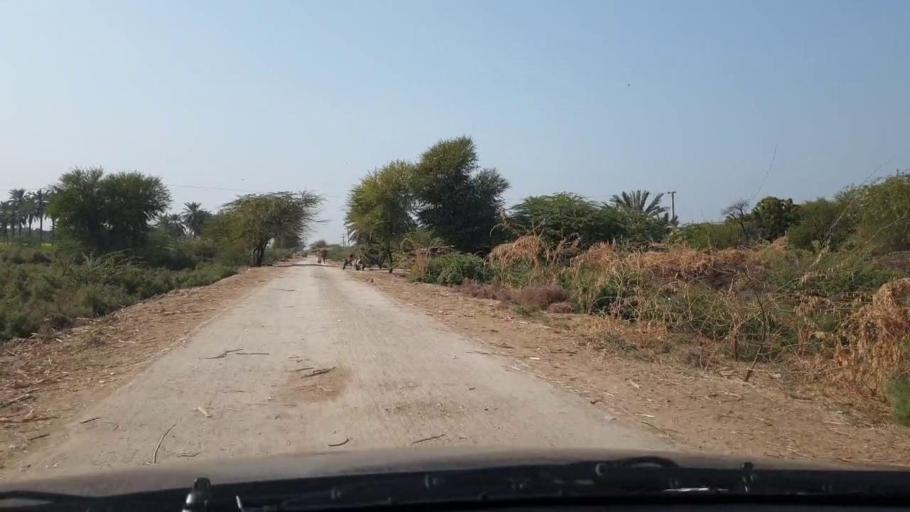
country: PK
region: Sindh
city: Jhol
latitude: 25.8923
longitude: 68.9330
